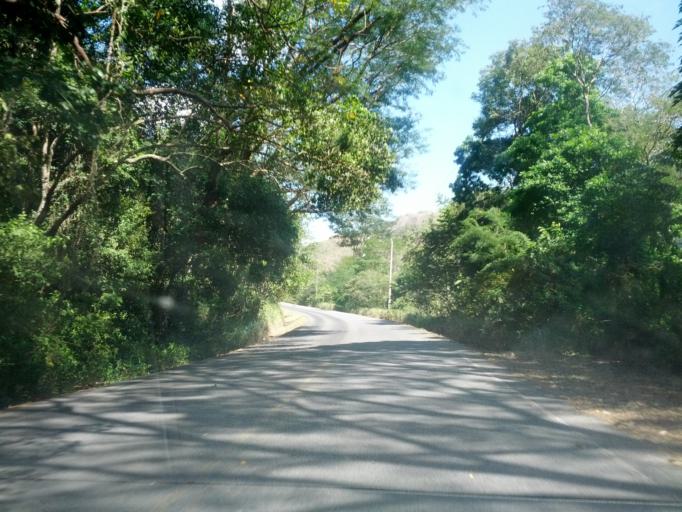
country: CR
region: Puntarenas
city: Buenos Aires
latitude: 8.9603
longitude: -83.3097
